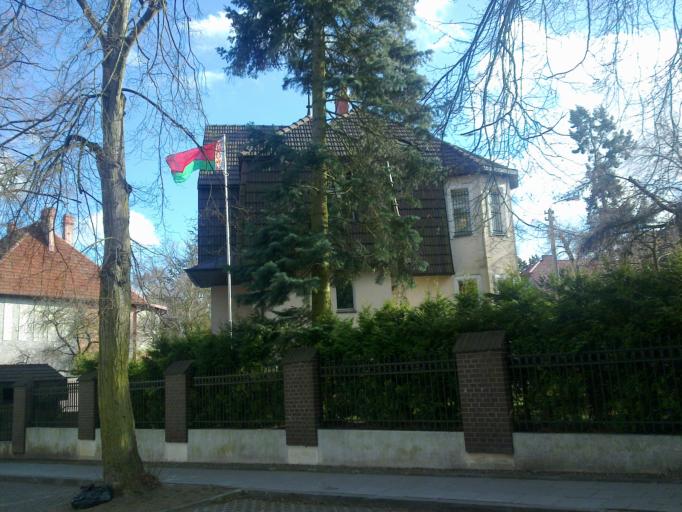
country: PL
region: Pomeranian Voivodeship
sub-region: Sopot
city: Sopot
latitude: 54.4039
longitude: 18.5629
